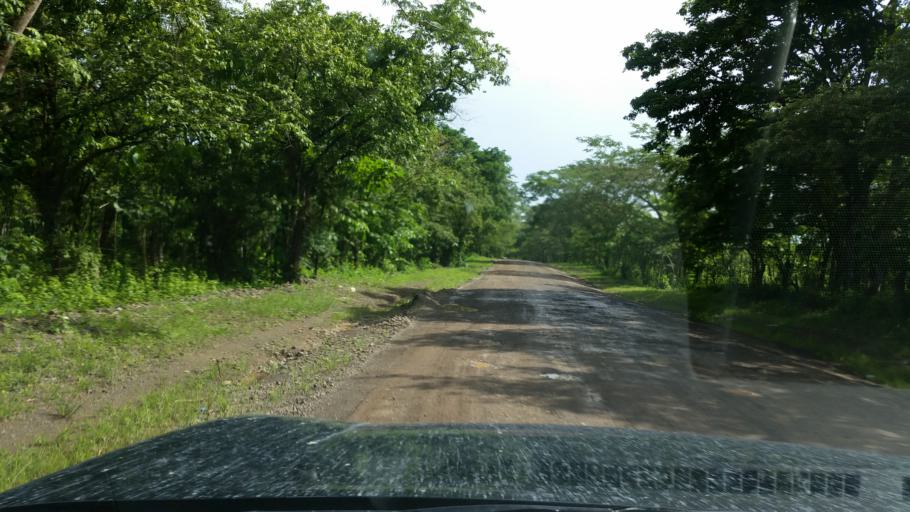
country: NI
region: Atlantico Norte (RAAN)
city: Siuna
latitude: 13.7033
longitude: -84.7791
